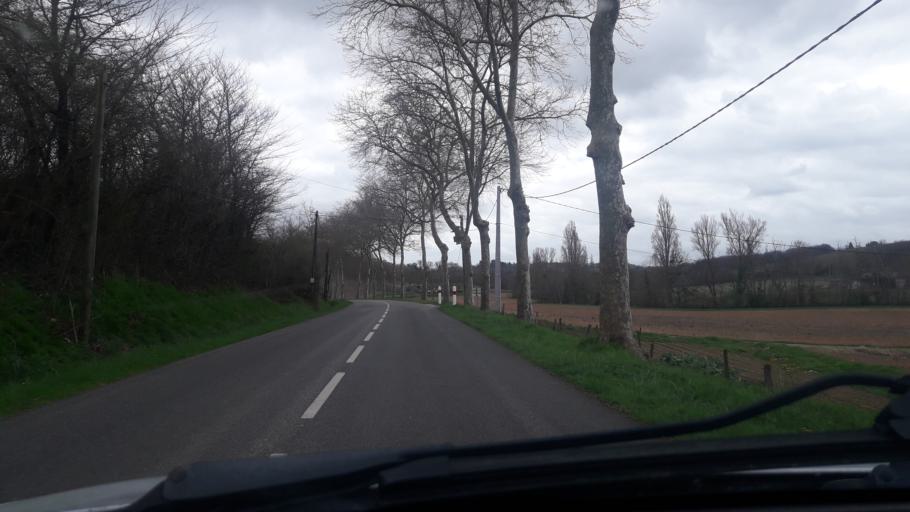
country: FR
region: Midi-Pyrenees
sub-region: Departement de la Haute-Garonne
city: Montesquieu-Volvestre
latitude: 43.2377
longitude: 1.2712
